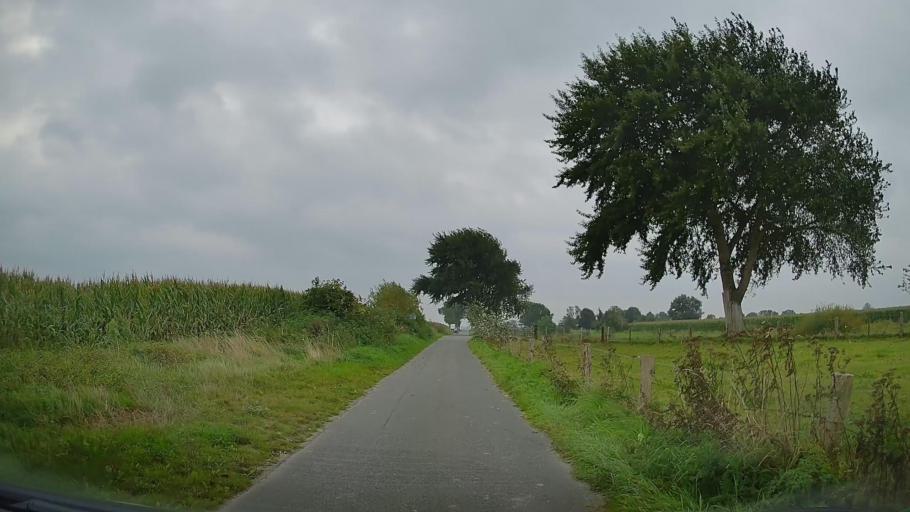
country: DE
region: Lower Saxony
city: Osterbruch
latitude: 53.8255
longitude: 8.9575
